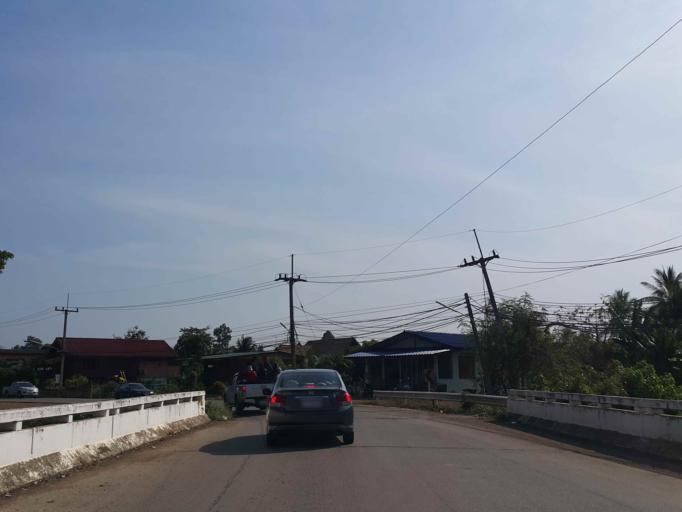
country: TH
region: Sukhothai
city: Thung Saliam
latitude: 17.3358
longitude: 99.5878
